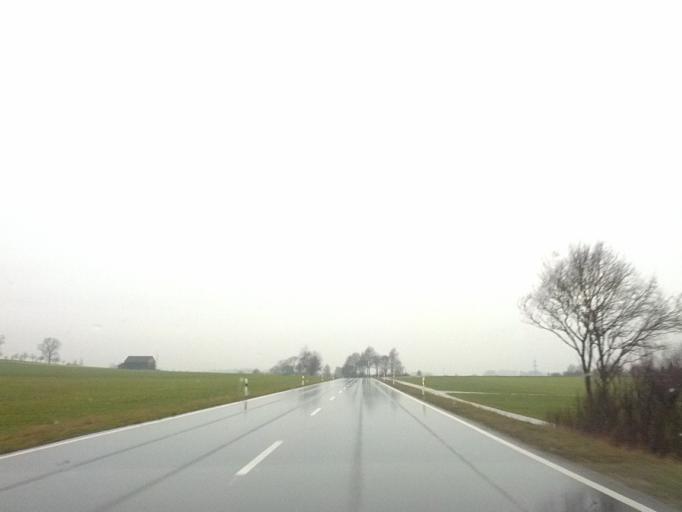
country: DE
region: Baden-Wuerttemberg
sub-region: Tuebingen Region
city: Ochsenhausen
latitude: 48.0735
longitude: 9.8939
